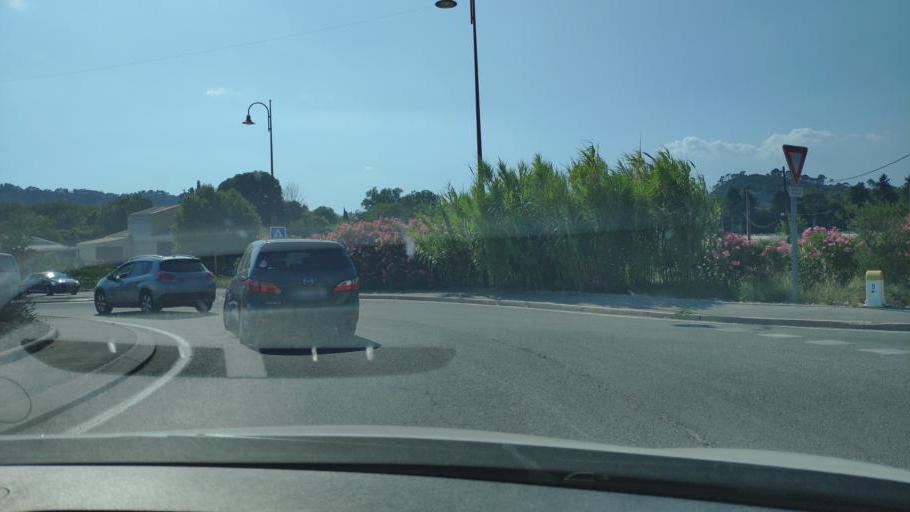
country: FR
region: Provence-Alpes-Cote d'Azur
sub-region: Departement du Var
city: Vidauban
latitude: 43.4228
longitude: 6.4270
